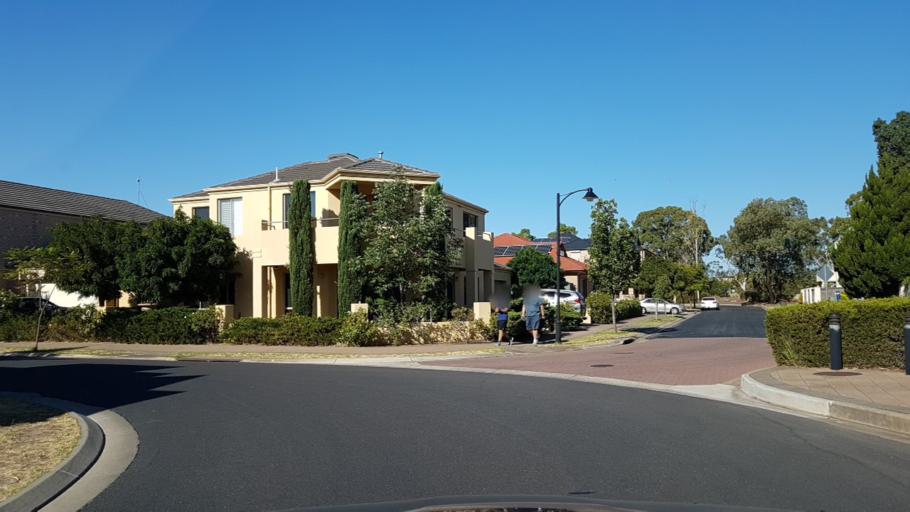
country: AU
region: South Australia
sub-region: Salisbury
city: Ingle Farm
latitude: -34.8128
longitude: 138.6108
